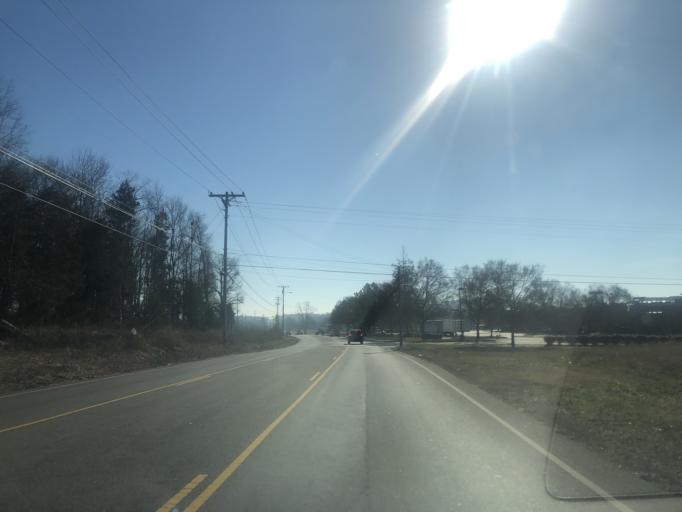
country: US
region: Tennessee
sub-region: Rutherford County
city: Smyrna
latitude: 35.9898
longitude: -86.5521
